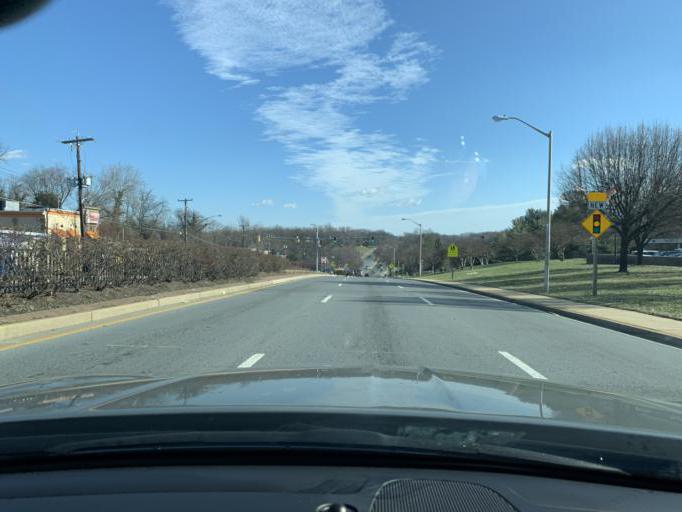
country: US
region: Maryland
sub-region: Prince George's County
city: Seat Pleasant
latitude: 38.8868
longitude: -76.8977
